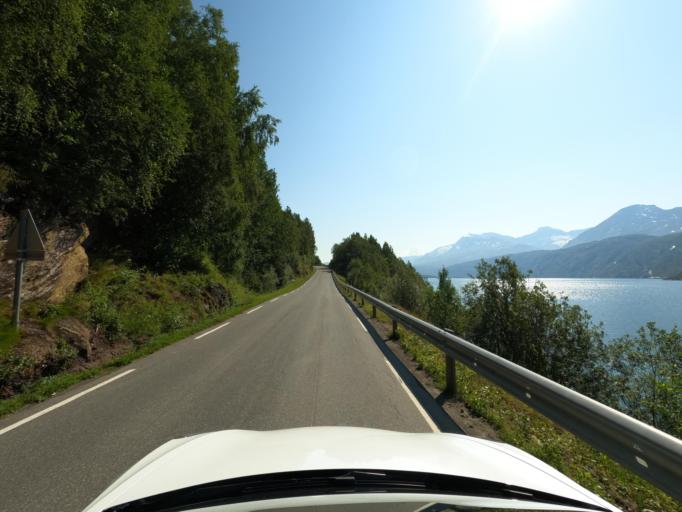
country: NO
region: Nordland
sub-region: Narvik
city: Narvik
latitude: 68.3618
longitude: 17.2624
